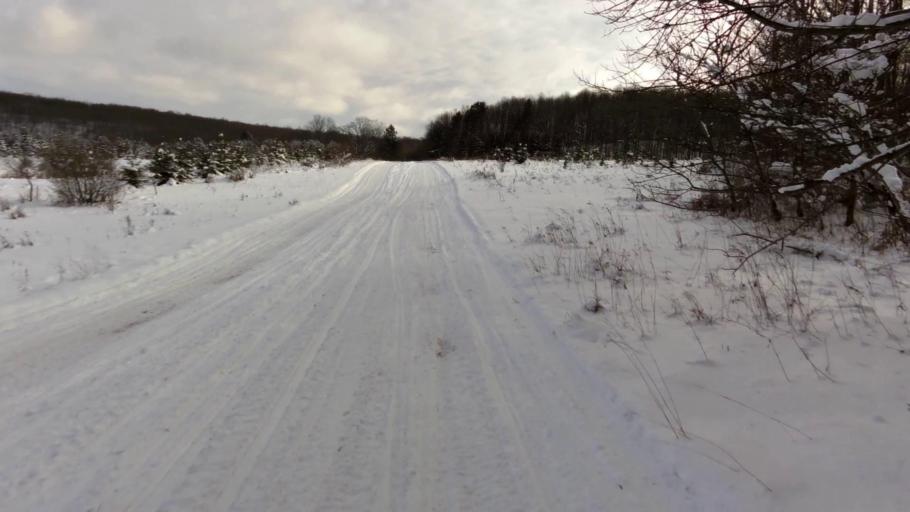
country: US
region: New York
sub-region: Cattaraugus County
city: Franklinville
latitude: 42.3119
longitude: -78.5343
